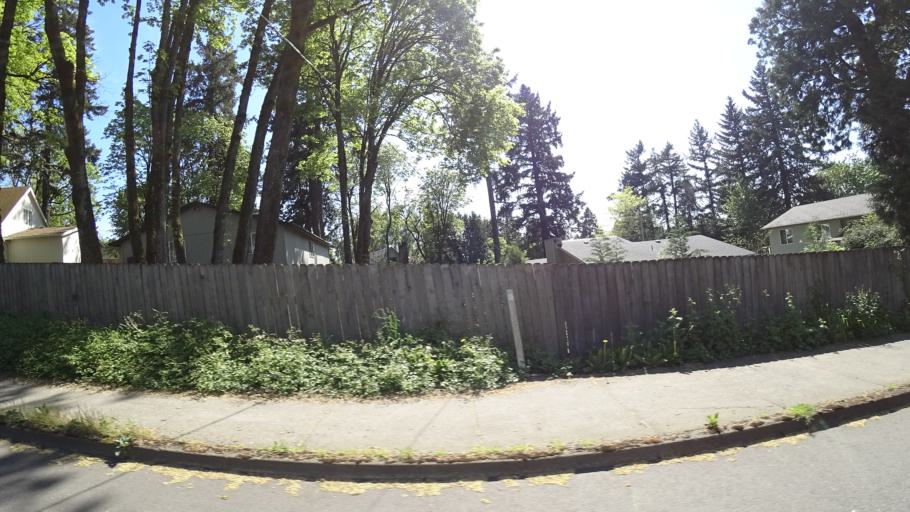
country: US
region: Oregon
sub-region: Clackamas County
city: Milwaukie
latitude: 45.4636
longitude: -122.6337
